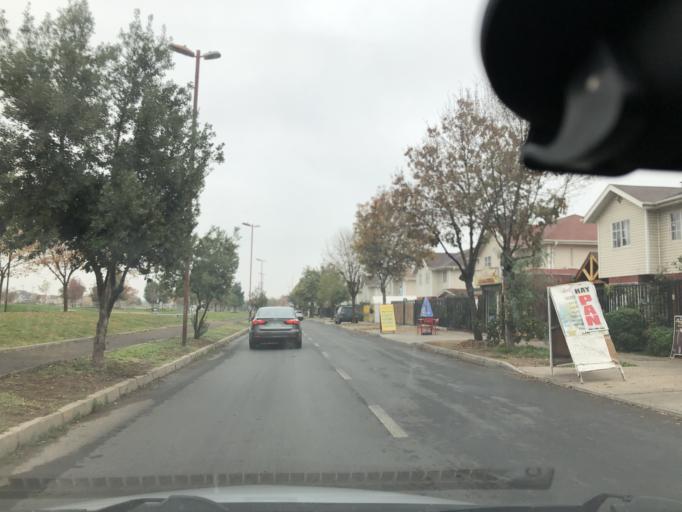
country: CL
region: Santiago Metropolitan
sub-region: Provincia de Cordillera
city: Puente Alto
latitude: -33.5954
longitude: -70.5880
